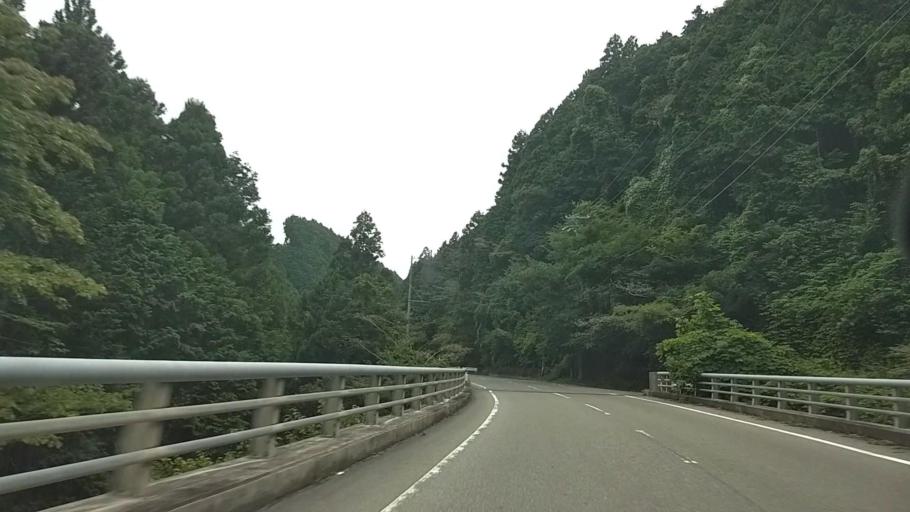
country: JP
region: Shizuoka
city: Fujinomiya
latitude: 35.1531
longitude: 138.5304
